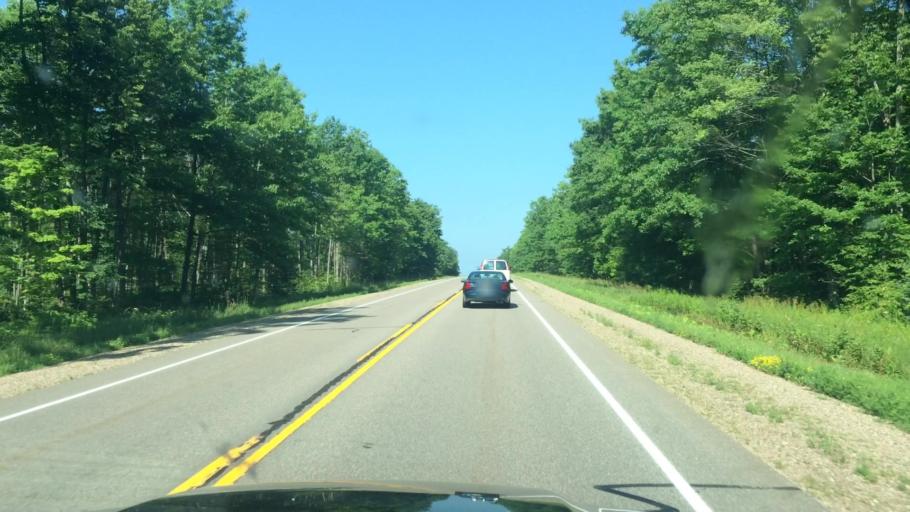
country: US
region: Wisconsin
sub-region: Langlade County
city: Antigo
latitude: 45.1470
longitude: -89.3825
